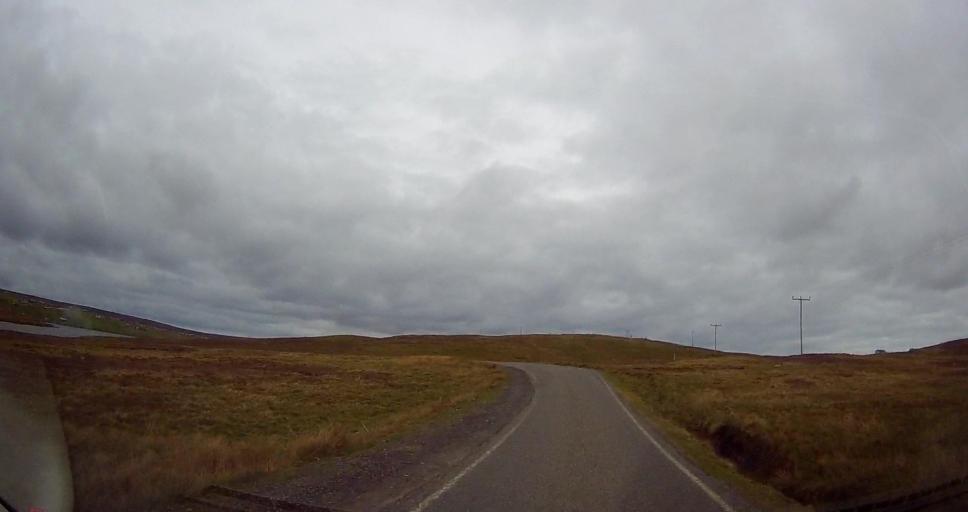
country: GB
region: Scotland
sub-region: Shetland Islands
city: Shetland
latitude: 60.6037
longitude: -1.0885
